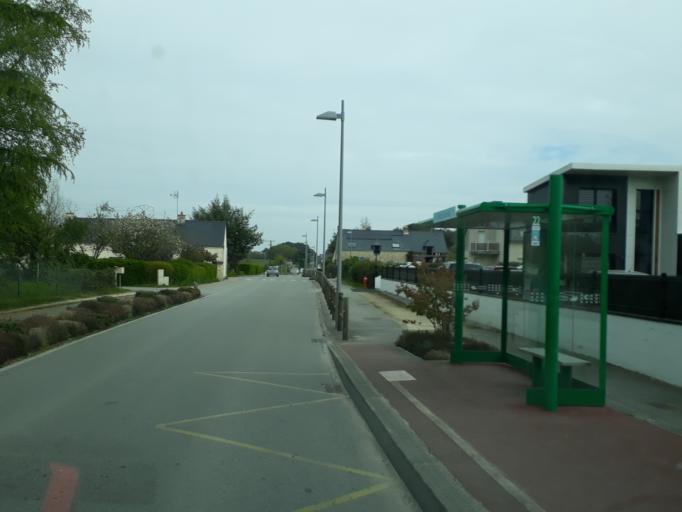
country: FR
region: Brittany
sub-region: Departement du Morbihan
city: Surzur
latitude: 47.5888
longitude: -2.6273
